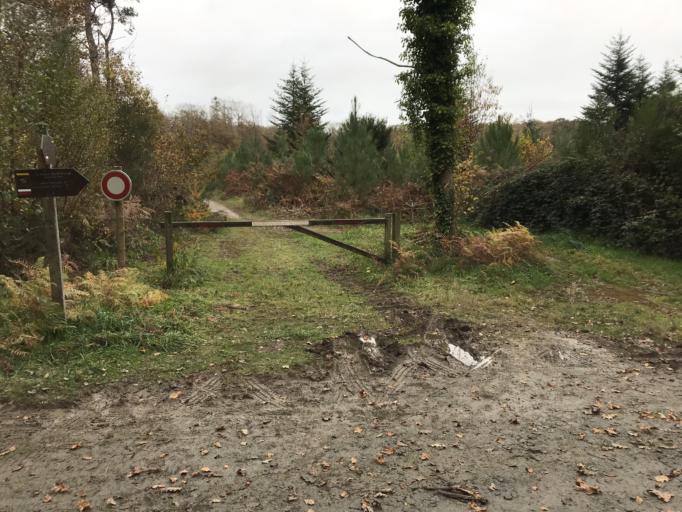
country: FR
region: Brittany
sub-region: Departement du Finistere
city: Hopital-Camfrout
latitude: 48.3352
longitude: -4.2089
